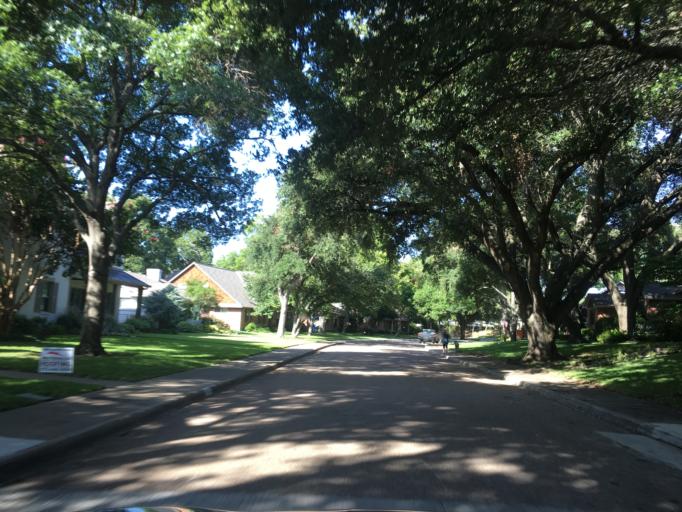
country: US
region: Texas
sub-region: Dallas County
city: Richardson
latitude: 32.8734
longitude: -96.7276
